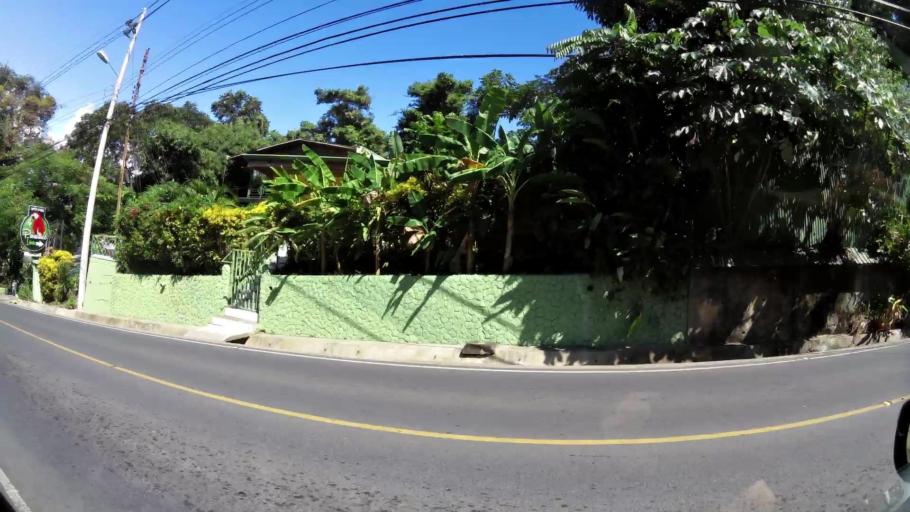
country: CR
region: Puntarenas
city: Quepos
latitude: 9.4113
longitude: -84.1550
